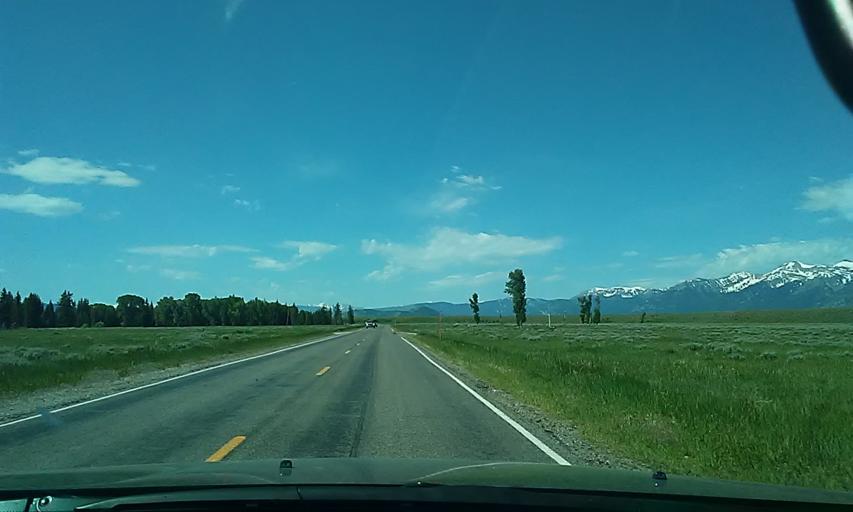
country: US
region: Wyoming
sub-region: Teton County
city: Jackson
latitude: 43.6101
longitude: -110.6850
